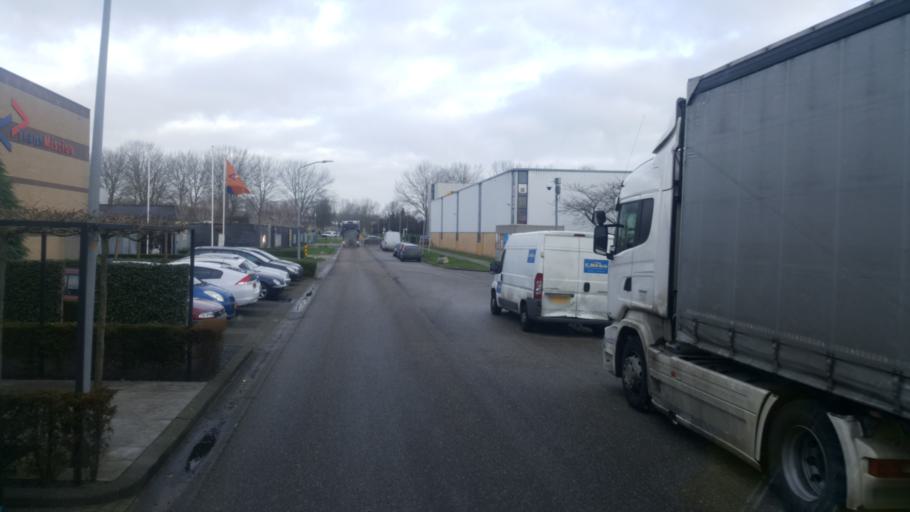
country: NL
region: Flevoland
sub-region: Gemeente Almere
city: Almere Stad
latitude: 52.3635
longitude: 5.1736
